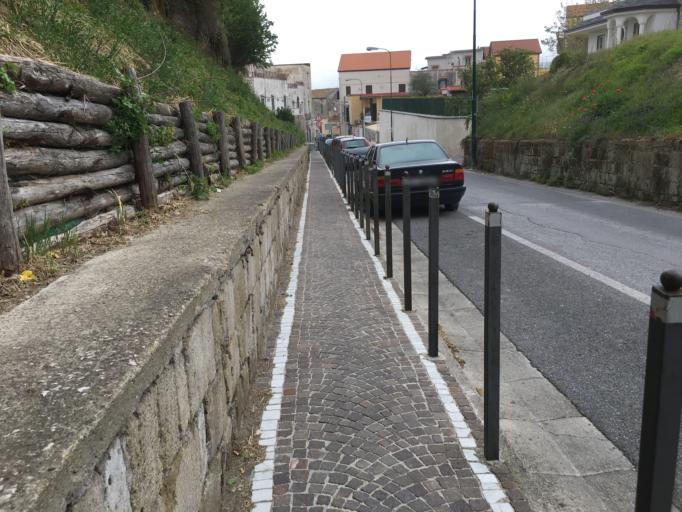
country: IT
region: Campania
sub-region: Provincia di Napoli
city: Torre Caracciolo
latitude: 40.8681
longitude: 14.1904
